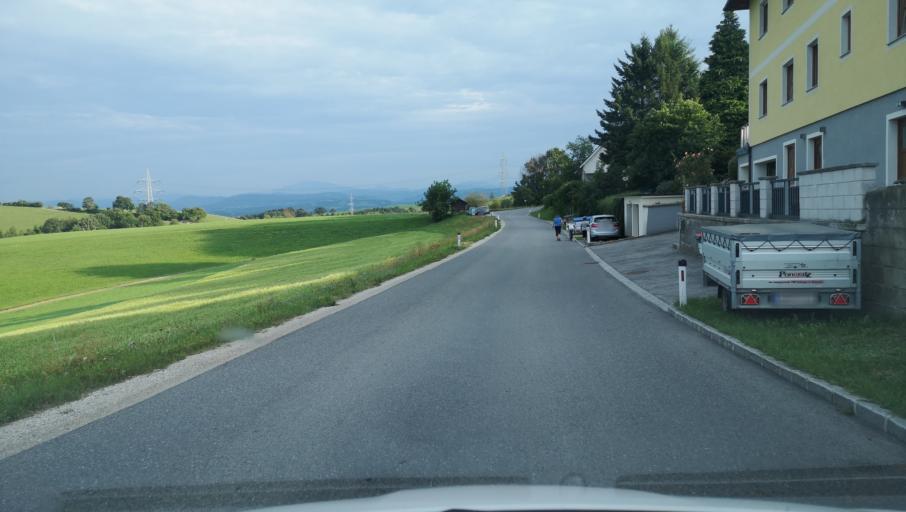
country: AT
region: Lower Austria
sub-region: Politischer Bezirk Amstetten
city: Sankt Georgen am Ybbsfelde
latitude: 48.1551
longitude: 14.9478
